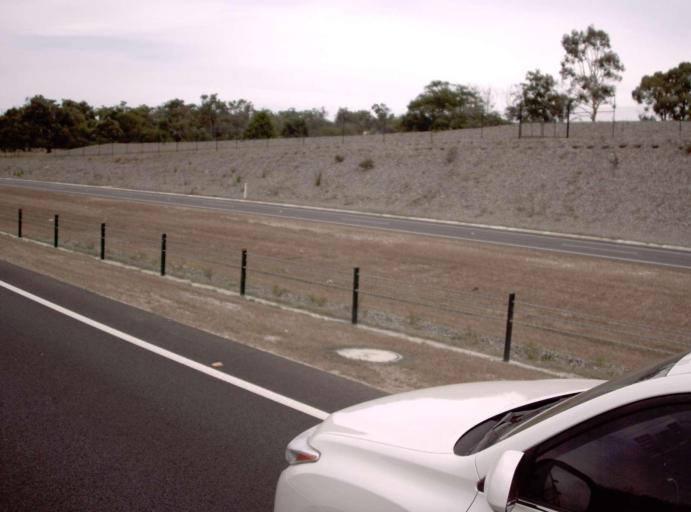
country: AU
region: Victoria
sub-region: Frankston
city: Langwarrin
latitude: -38.1699
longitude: 145.1638
